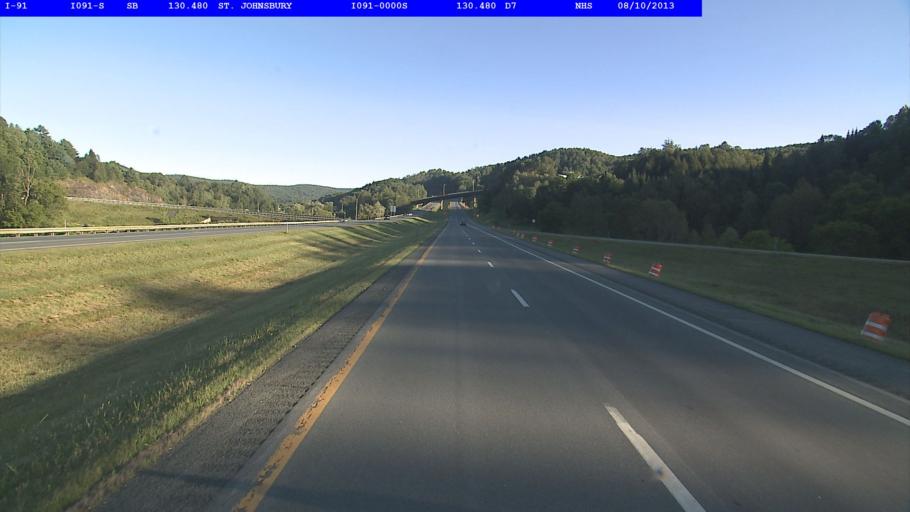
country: US
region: Vermont
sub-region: Caledonia County
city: St Johnsbury
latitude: 44.4260
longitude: -72.0335
